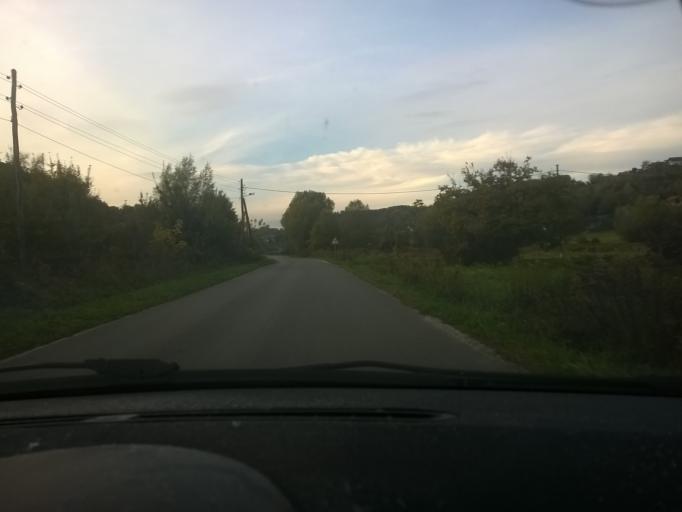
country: HR
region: Krapinsko-Zagorska
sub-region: Grad Krapina
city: Krapina
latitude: 46.1167
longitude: 15.8617
